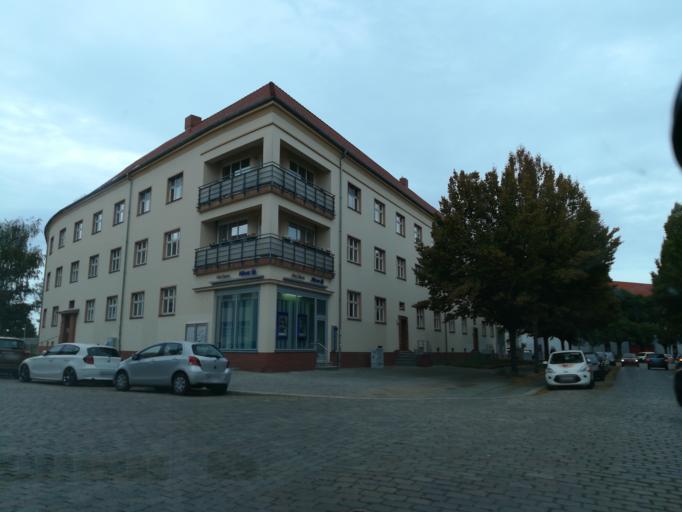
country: DE
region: Saxony-Anhalt
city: Magdeburg
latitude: 52.1375
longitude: 11.6193
